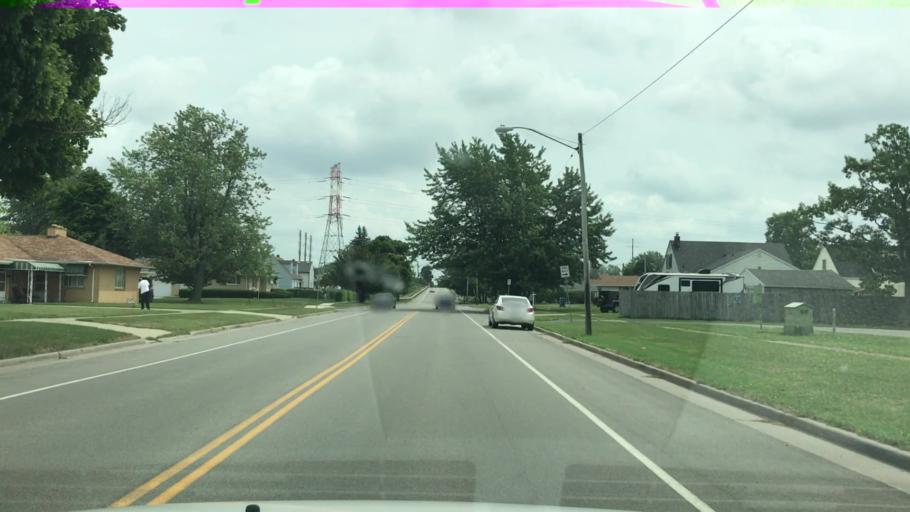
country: US
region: New York
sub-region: Erie County
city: Cheektowaga
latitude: 42.9188
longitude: -78.7724
